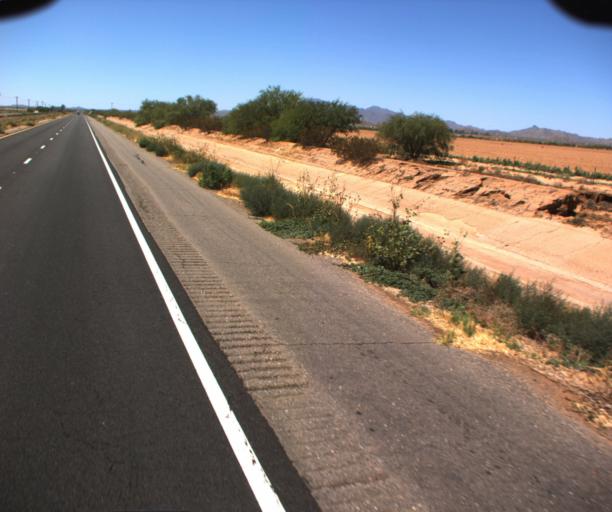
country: US
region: Arizona
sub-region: Pinal County
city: Maricopa
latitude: 32.9219
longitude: -112.0497
